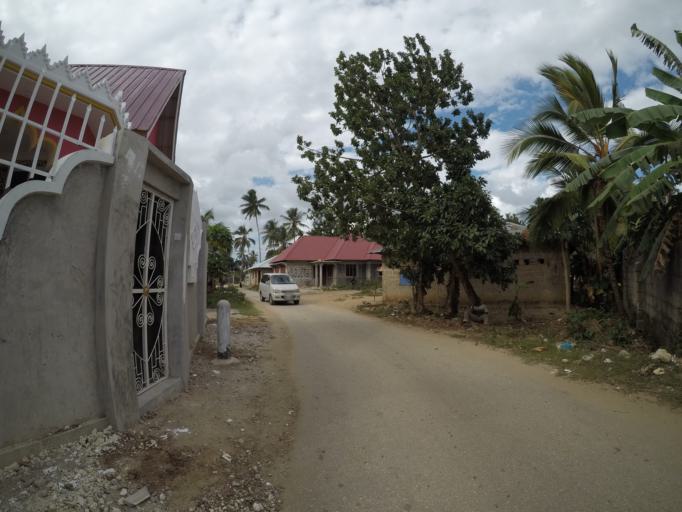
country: TZ
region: Zanzibar Central/South
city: Koani
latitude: -6.1948
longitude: 39.2642
